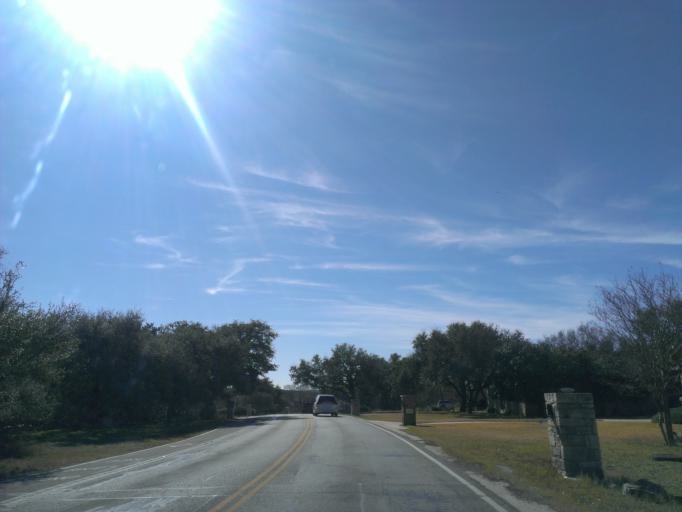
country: US
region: Texas
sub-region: Travis County
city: Lakeway
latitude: 30.3704
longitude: -97.9775
